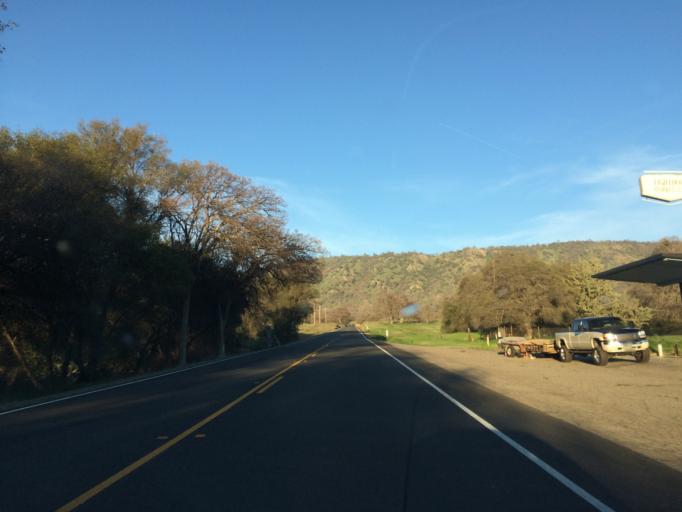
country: US
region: California
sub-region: Mariposa County
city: Mariposa
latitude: 37.4414
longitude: -120.0824
